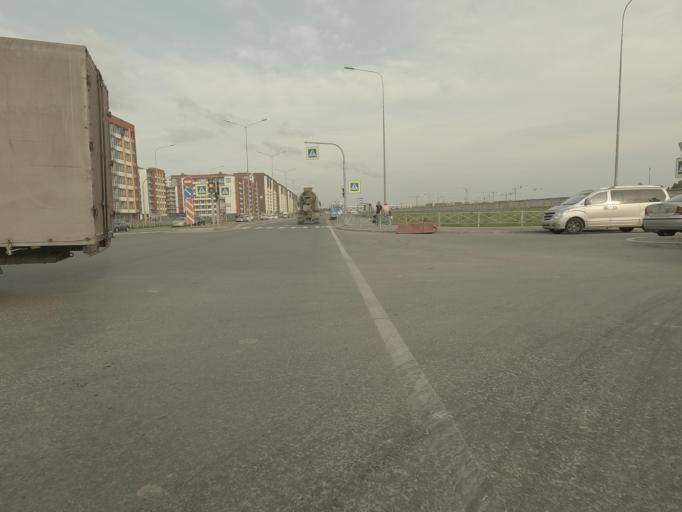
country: RU
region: St.-Petersburg
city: Sosnovaya Polyana
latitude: 59.8394
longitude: 30.0968
